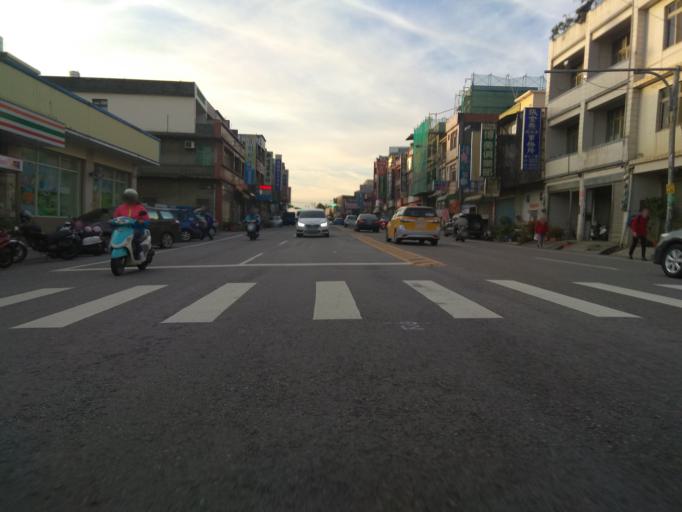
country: TW
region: Taiwan
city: Taoyuan City
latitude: 24.9880
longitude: 121.1817
